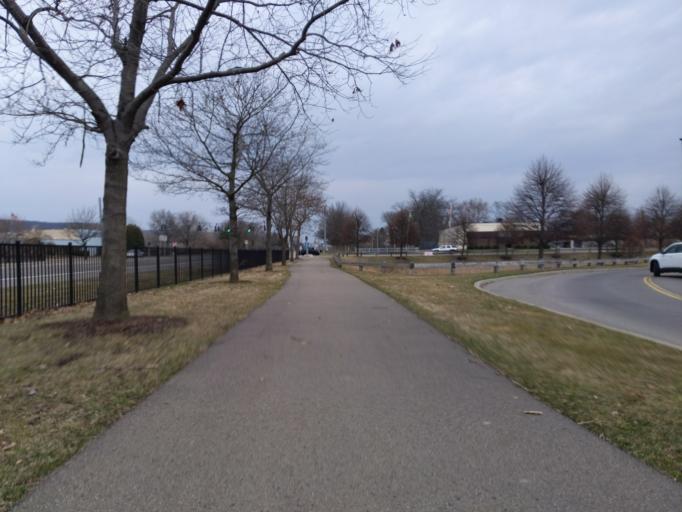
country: US
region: New York
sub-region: Chemung County
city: Elmira
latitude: 42.1054
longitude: -76.8106
